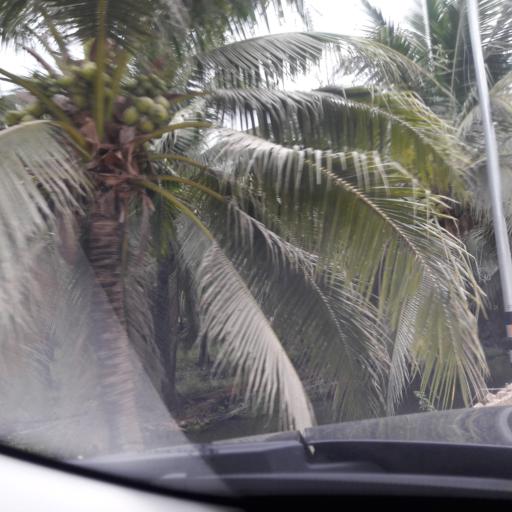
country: TH
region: Ratchaburi
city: Damnoen Saduak
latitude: 13.5782
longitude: 99.9516
